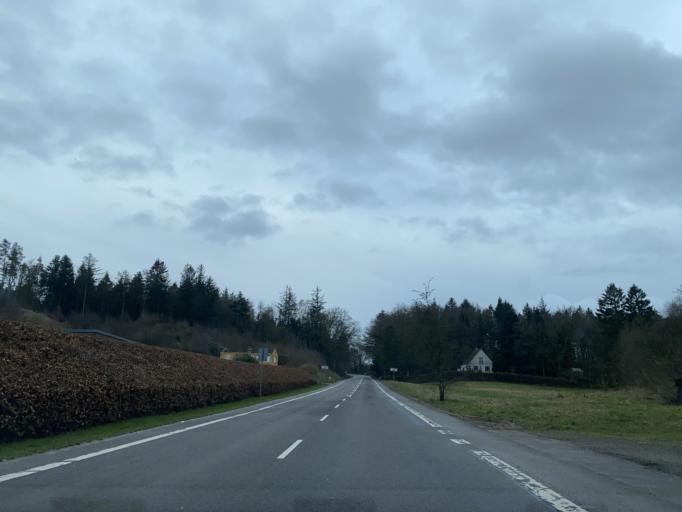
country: DK
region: Central Jutland
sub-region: Viborg Kommune
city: Bjerringbro
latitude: 56.3007
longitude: 9.5981
